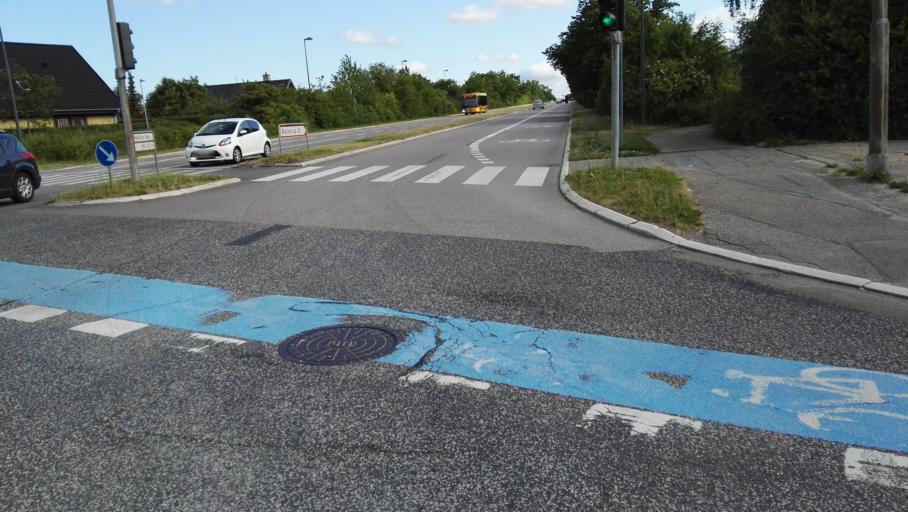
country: DK
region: Capital Region
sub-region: Ballerup Kommune
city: Ballerup
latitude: 55.7123
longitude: 12.3562
